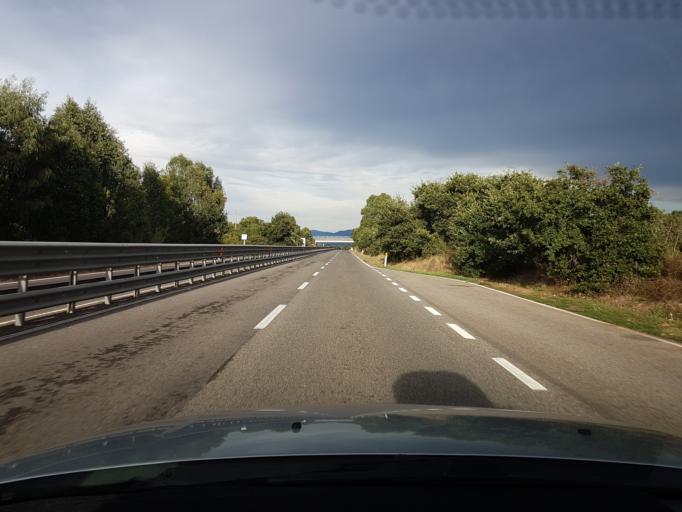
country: IT
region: Sardinia
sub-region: Provincia di Oristano
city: Ghilarza
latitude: 40.1153
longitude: 8.8273
